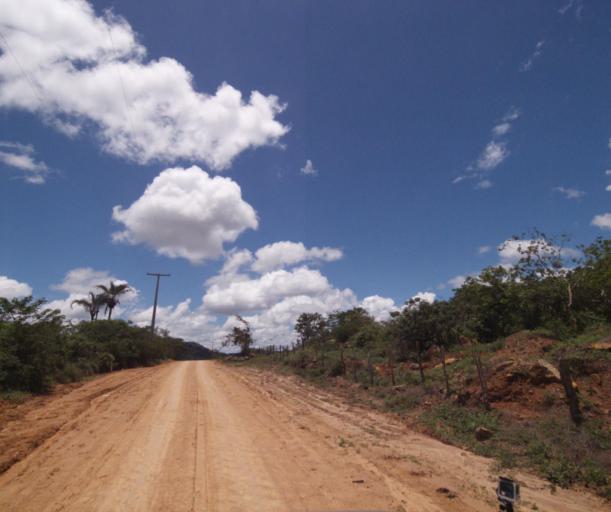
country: BR
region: Bahia
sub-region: Pocoes
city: Pocoes
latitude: -14.3821
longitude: -40.4143
